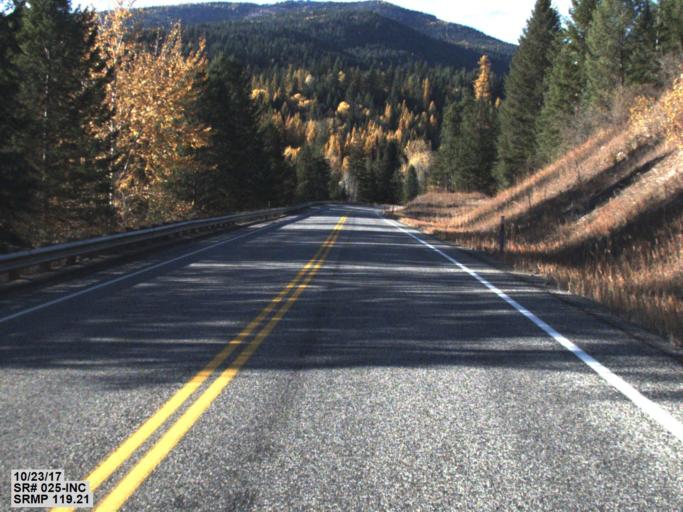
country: CA
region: British Columbia
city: Rossland
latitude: 48.9740
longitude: -117.8174
